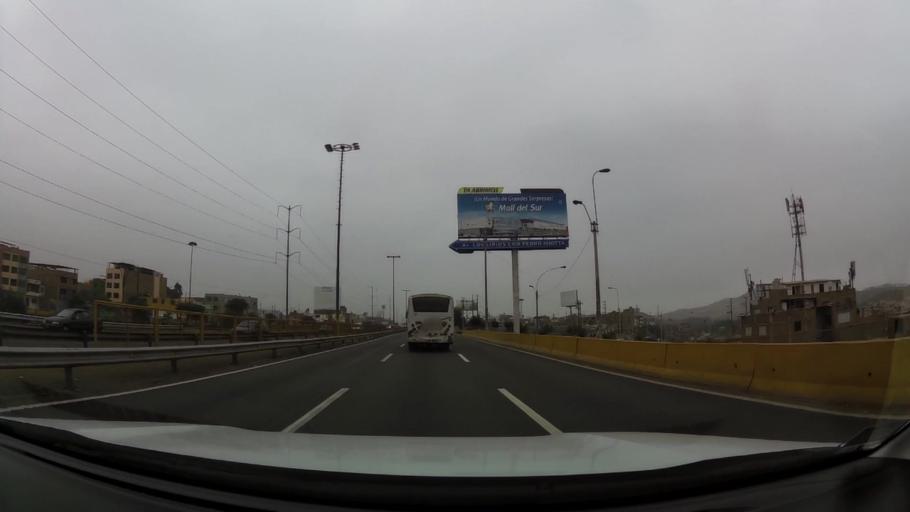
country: PE
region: Lima
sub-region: Lima
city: Surco
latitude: -12.1696
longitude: -76.9800
